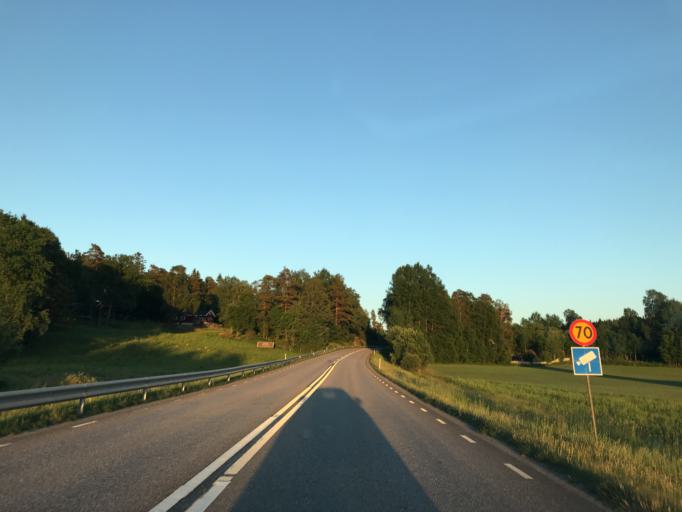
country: SE
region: Vaestra Goetaland
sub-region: Harryda Kommun
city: Ravlanda
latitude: 57.5524
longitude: 12.5268
